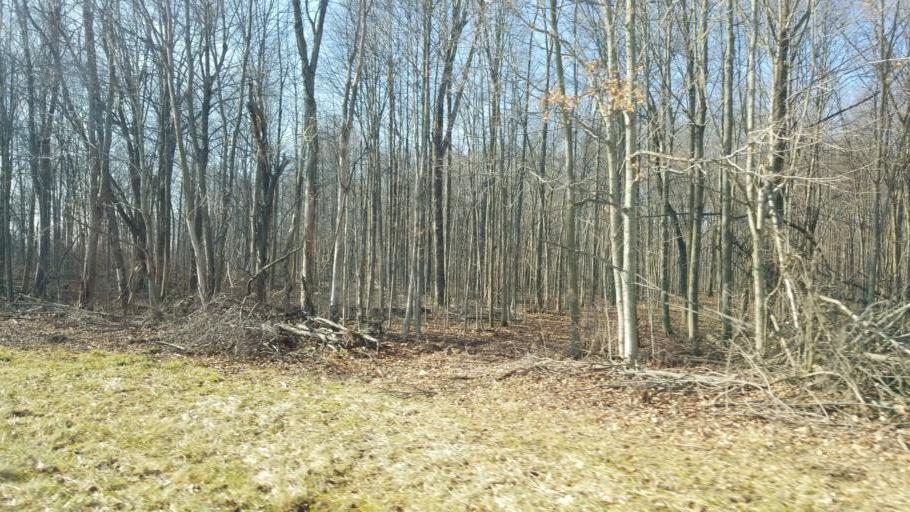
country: US
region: Ohio
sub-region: Seneca County
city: Tiffin
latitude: 41.1183
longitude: -83.1120
